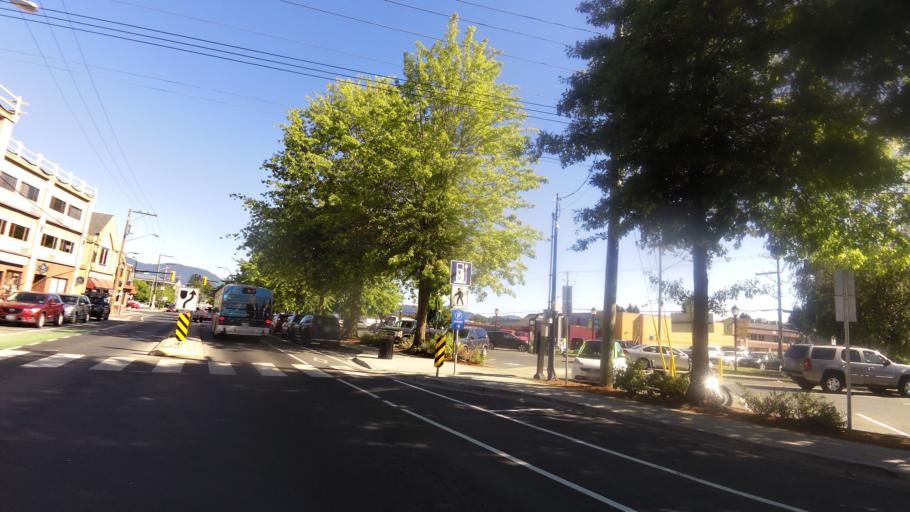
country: CA
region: British Columbia
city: Duncan
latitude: 48.7785
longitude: -123.7072
